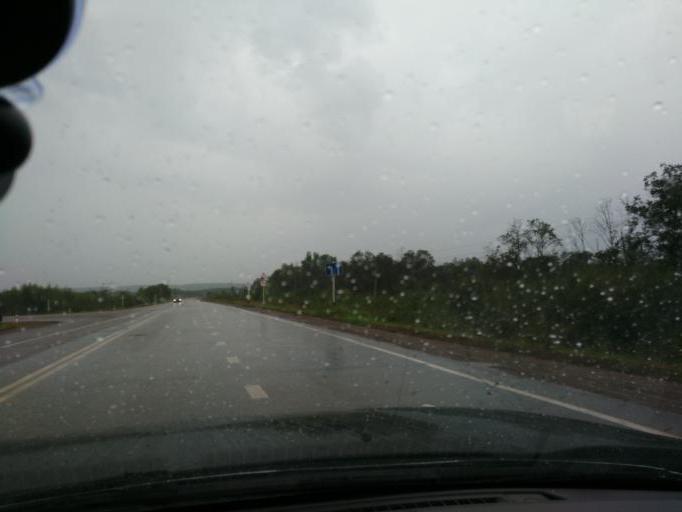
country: RU
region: Perm
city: Barda
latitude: 56.9439
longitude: 55.6163
